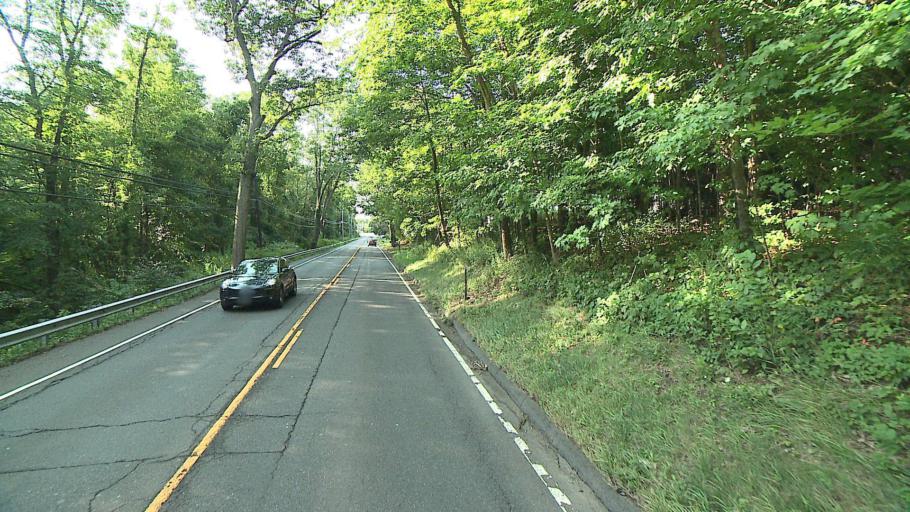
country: US
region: Connecticut
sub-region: Fairfield County
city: Georgetown
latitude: 41.2432
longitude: -73.4339
